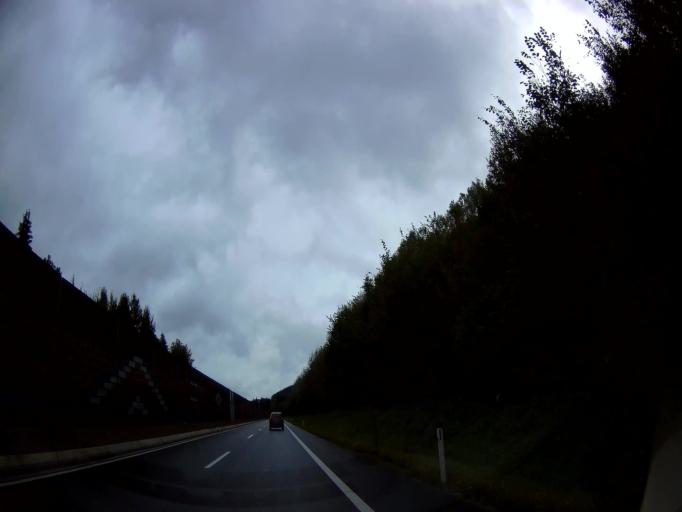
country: AT
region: Styria
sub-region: Politischer Bezirk Liezen
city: Rottenmann
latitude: 47.5224
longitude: 14.3471
